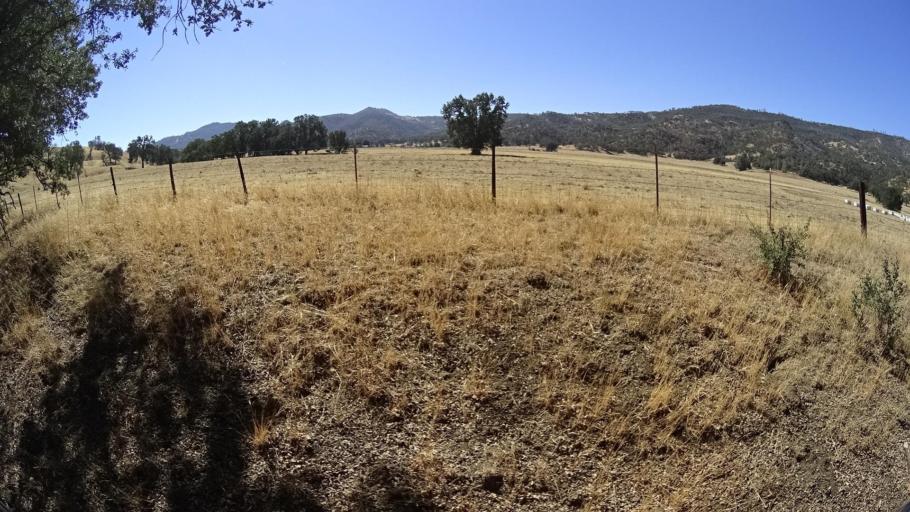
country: US
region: California
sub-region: Fresno County
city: Coalinga
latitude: 36.1836
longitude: -120.6950
